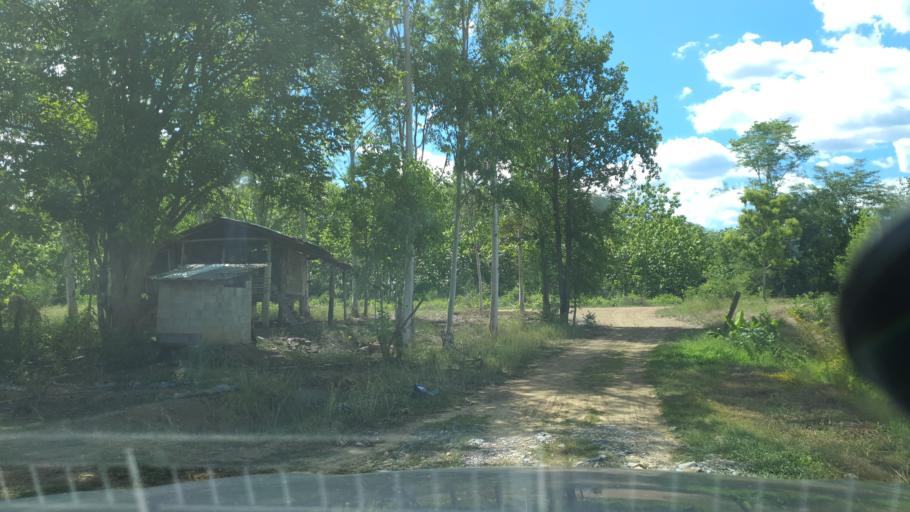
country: TH
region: Sukhothai
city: Thung Saliam
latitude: 17.3405
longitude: 99.4386
